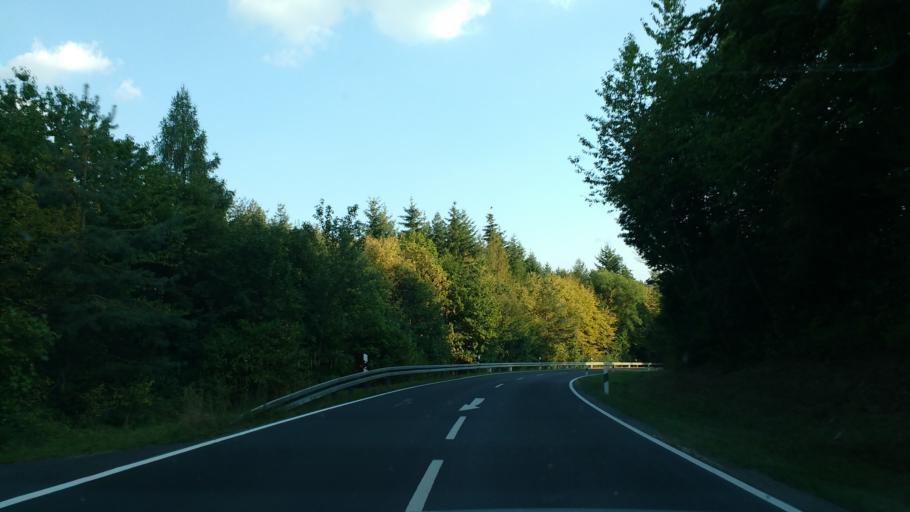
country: DE
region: Bavaria
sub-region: Regierungsbezirk Unterfranken
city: Elfershausen
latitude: 50.1710
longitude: 9.9610
